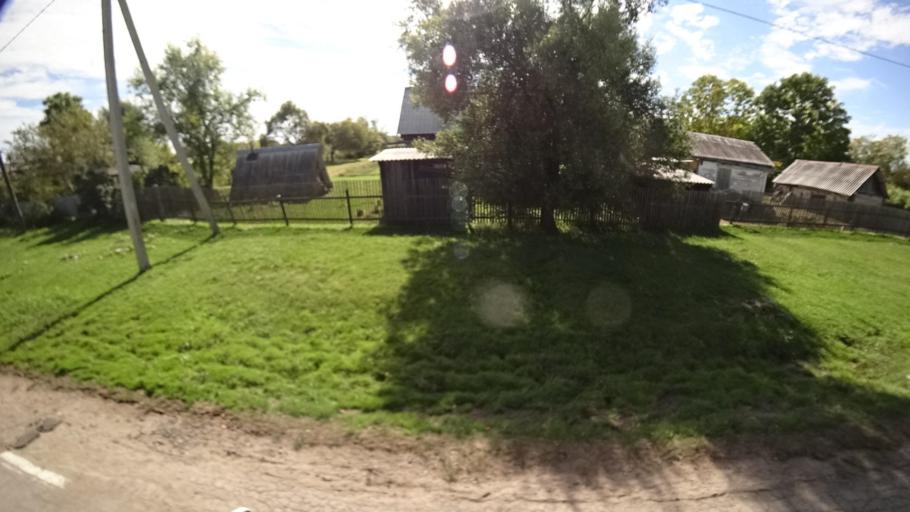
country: RU
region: Primorskiy
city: Yakovlevka
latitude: 44.4274
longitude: 133.5733
